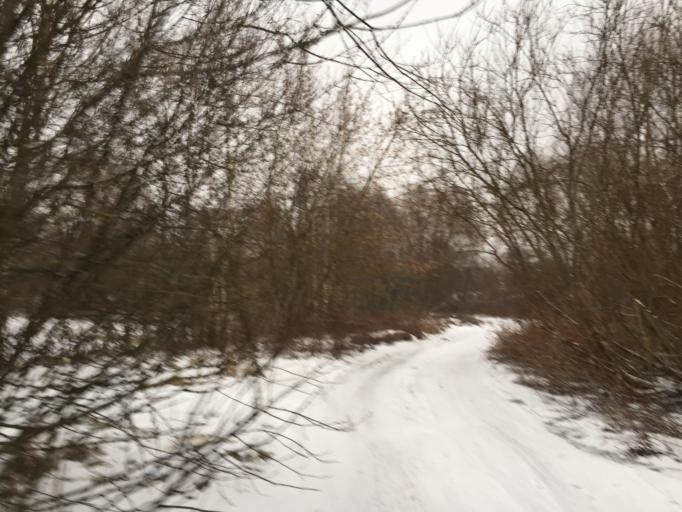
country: LV
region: Riga
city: Riga
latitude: 56.9176
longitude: 24.1425
